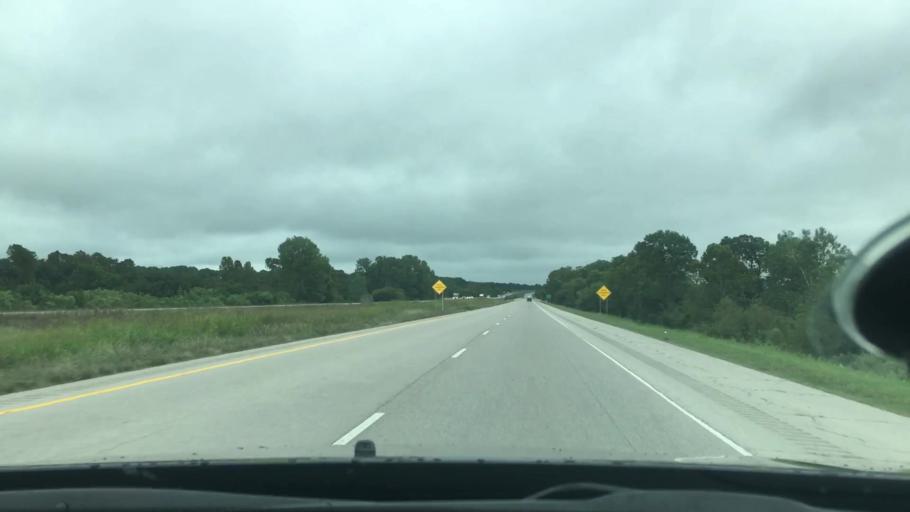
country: US
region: Oklahoma
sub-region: Okfuskee County
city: Okemah
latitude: 35.3916
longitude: -96.4064
